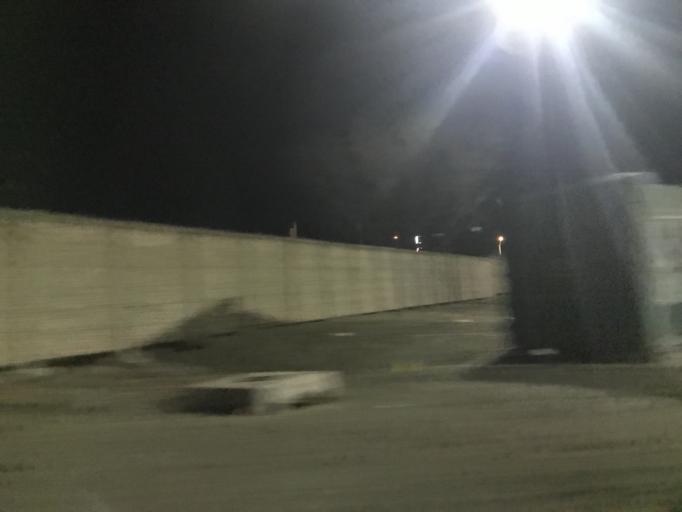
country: US
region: Texas
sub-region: Taylor County
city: Abilene
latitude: 32.4804
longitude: -99.6963
